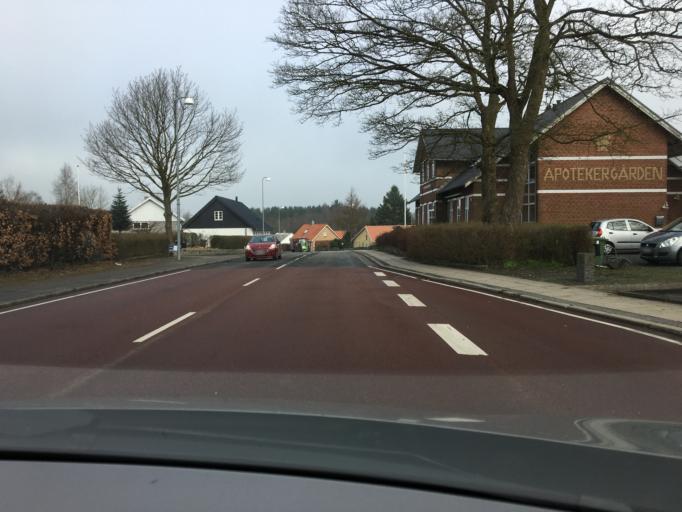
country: DK
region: South Denmark
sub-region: Vejle Kommune
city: Jelling
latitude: 55.8168
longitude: 9.3472
